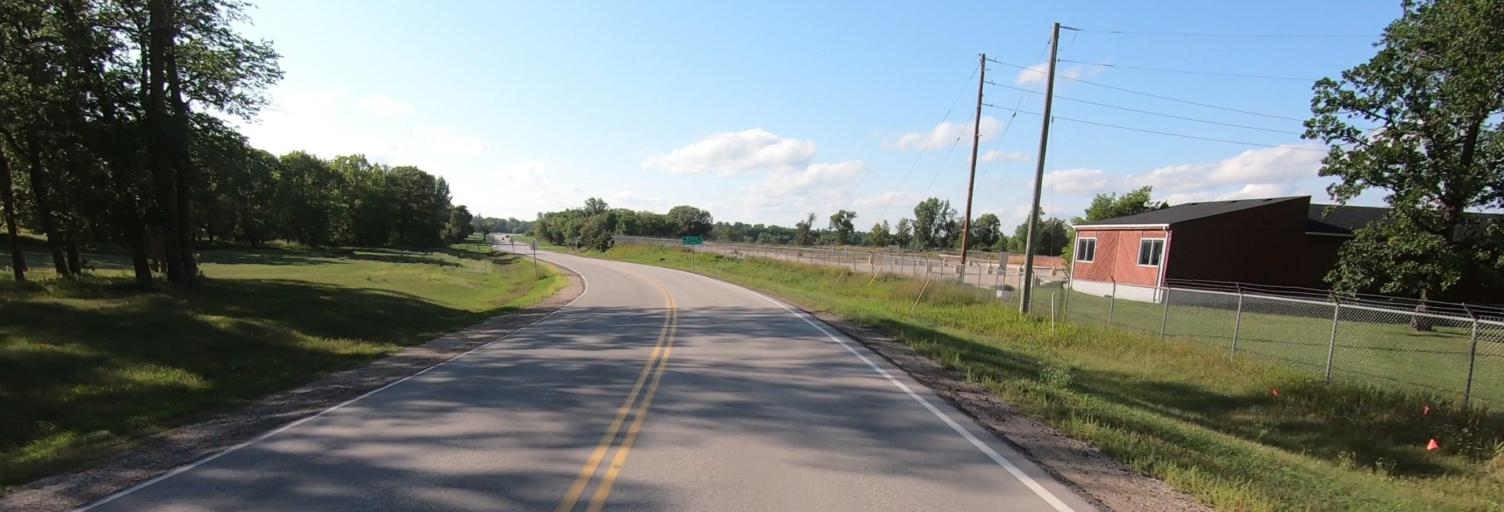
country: CA
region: Manitoba
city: Selkirk
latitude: 50.1337
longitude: -96.8542
